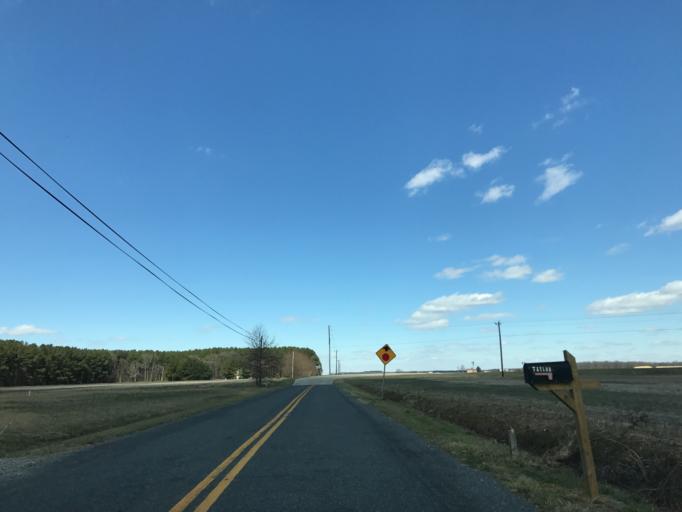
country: US
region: Maryland
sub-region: Caroline County
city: Greensboro
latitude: 39.1000
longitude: -75.8750
